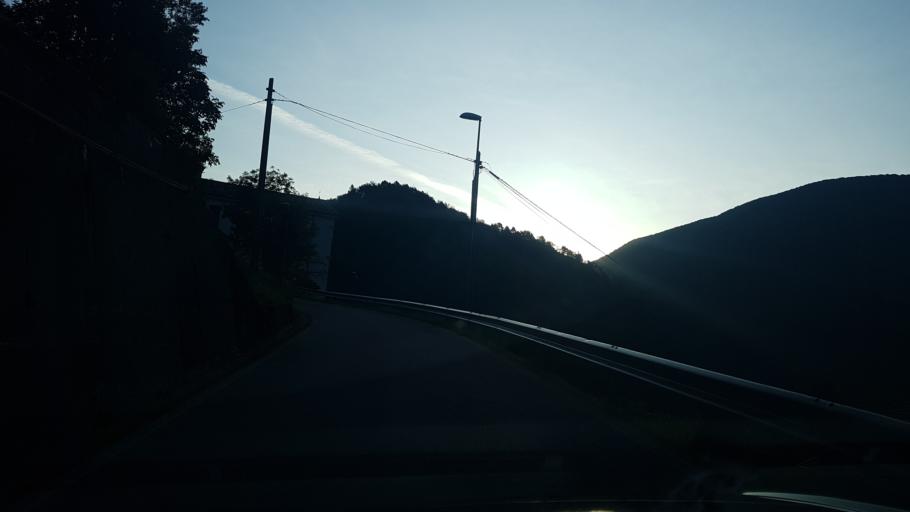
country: IT
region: Friuli Venezia Giulia
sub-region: Provincia di Pordenone
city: Frisanco
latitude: 46.2549
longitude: 12.7360
